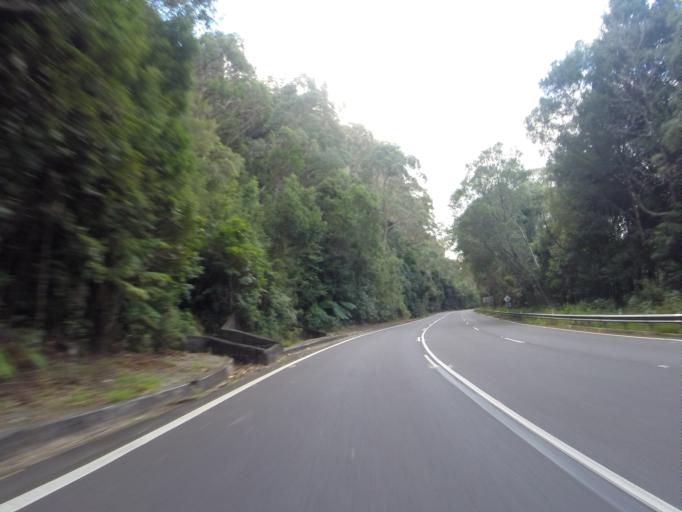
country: AU
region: New South Wales
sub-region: Shellharbour
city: Calderwood
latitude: -34.5580
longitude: 150.6428
